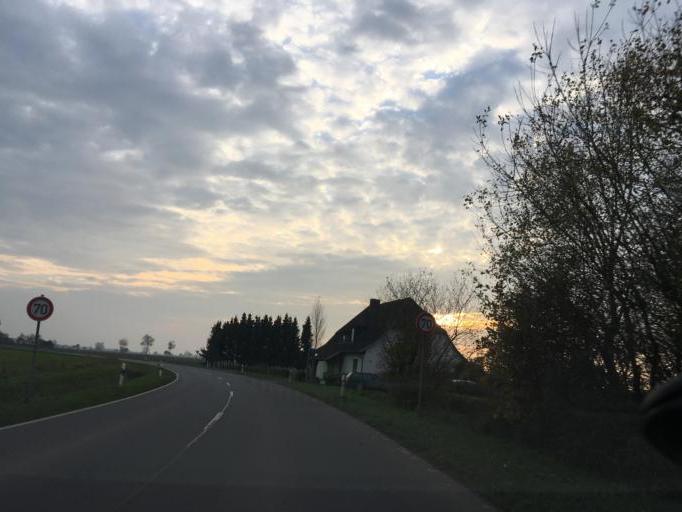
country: DE
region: Lower Saxony
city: Bergen
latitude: 52.8489
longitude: 9.9736
